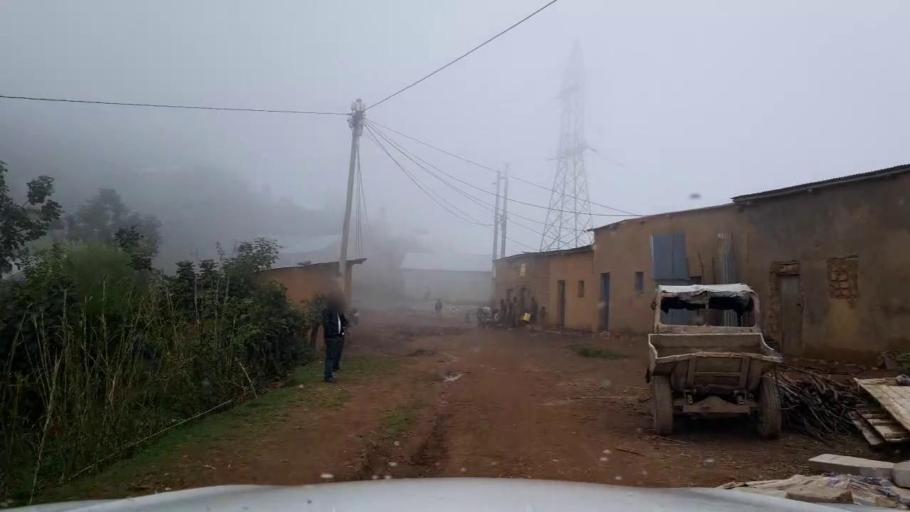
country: RW
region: Northern Province
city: Musanze
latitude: -1.5968
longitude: 29.7923
